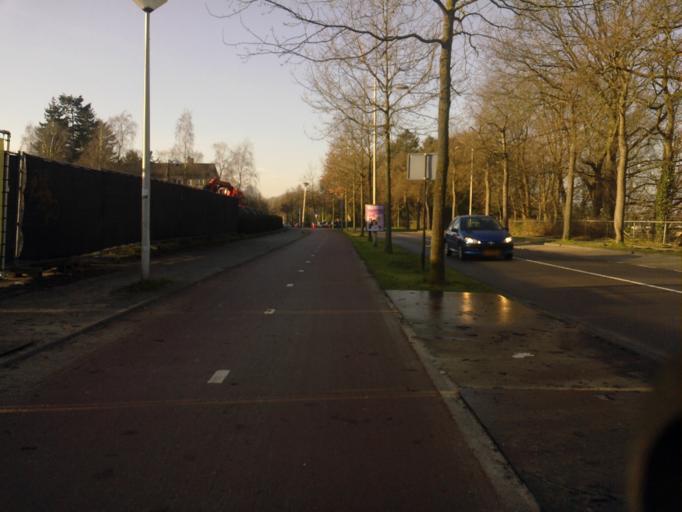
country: NL
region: Utrecht
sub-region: Gemeente Amersfoort
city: Amersfoort
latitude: 52.1526
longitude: 5.3646
